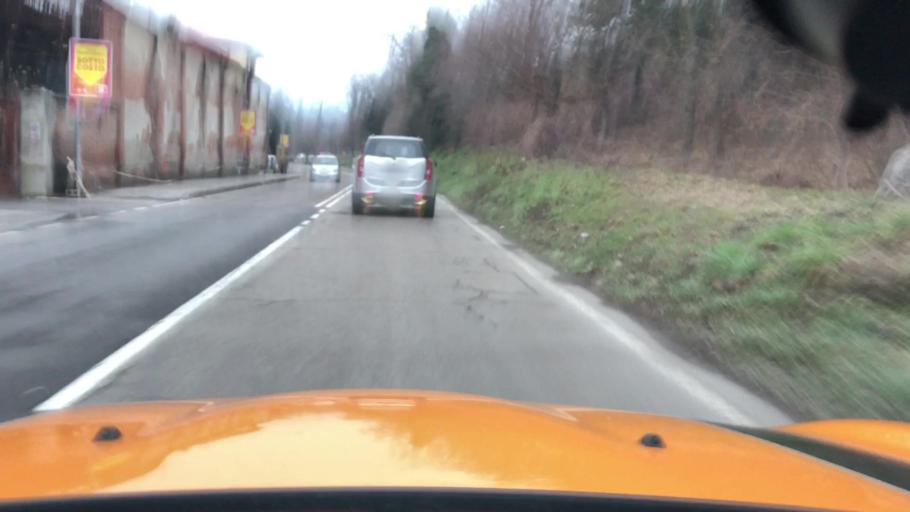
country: IT
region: Lombardy
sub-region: Provincia di Como
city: Capiago-Intimiano-Olmeda
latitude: 45.7525
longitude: 9.1293
